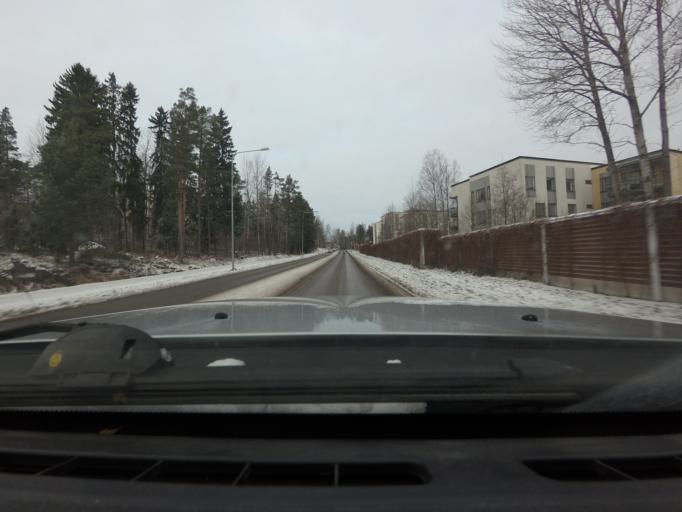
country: FI
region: Uusimaa
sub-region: Helsinki
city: Kilo
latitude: 60.2311
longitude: 24.7757
